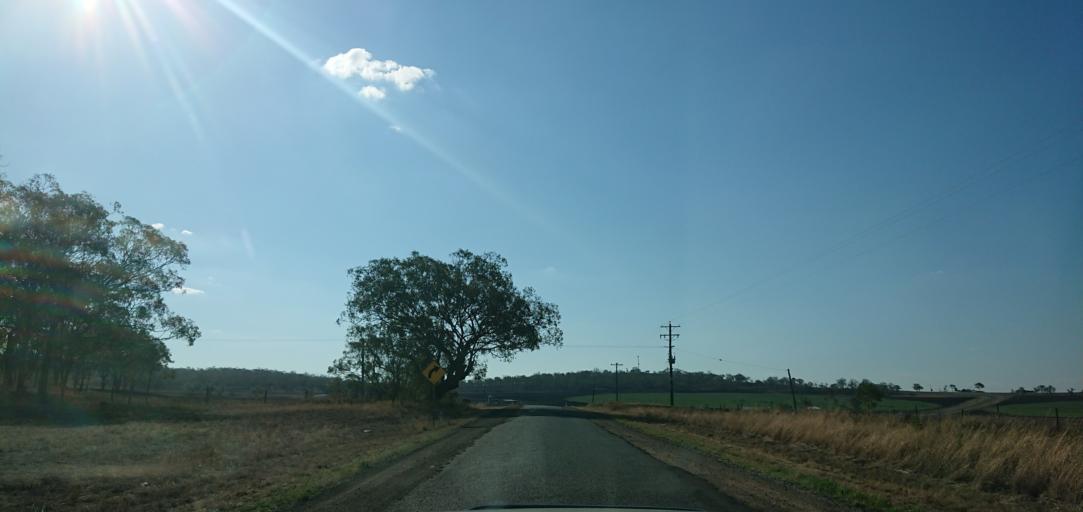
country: AU
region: Queensland
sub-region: Toowoomba
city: Westbrook
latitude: -27.7123
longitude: 151.7171
